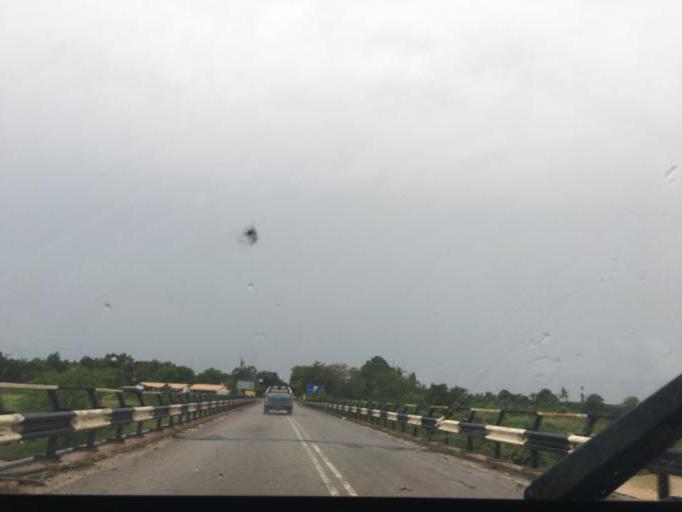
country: MY
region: Kedah
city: Sungai Petani
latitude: 5.6130
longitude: 100.6394
